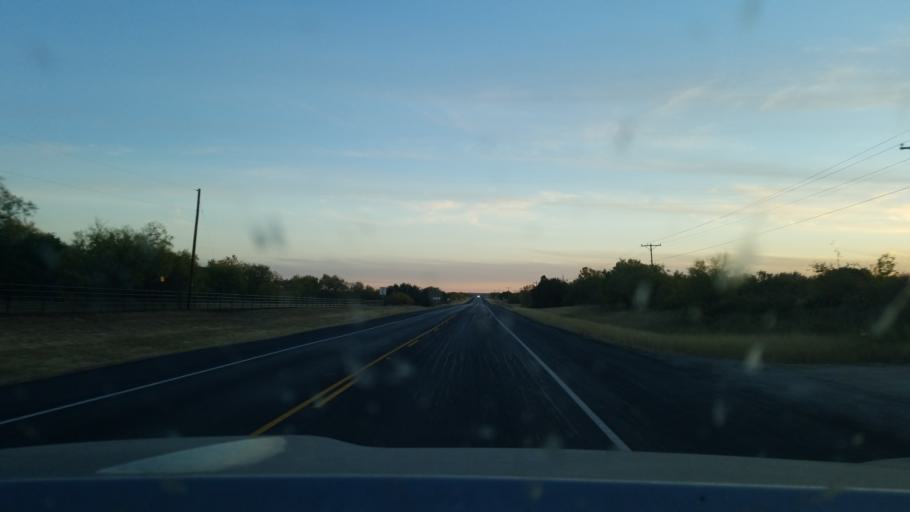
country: US
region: Texas
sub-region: Stephens County
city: Breckenridge
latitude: 32.6762
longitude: -98.9020
